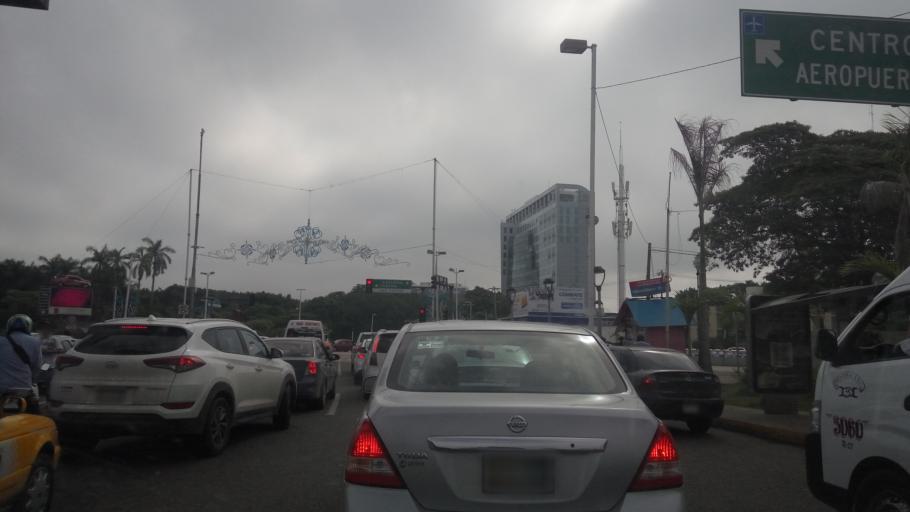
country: MX
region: Tabasco
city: Villahermosa
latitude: 17.9973
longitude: -92.9412
